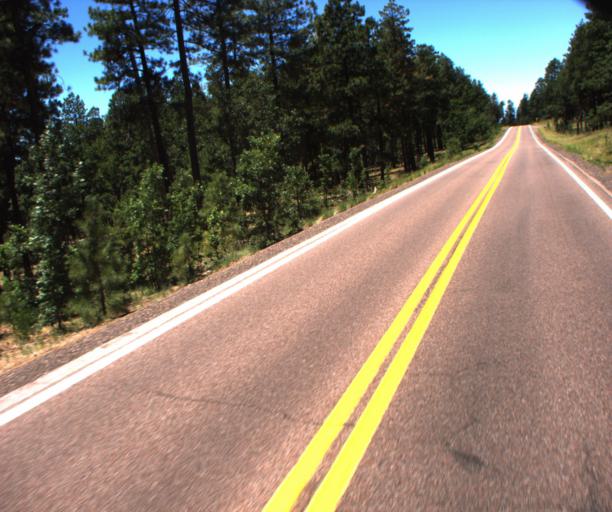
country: US
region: Arizona
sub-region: Gila County
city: Pine
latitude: 34.4418
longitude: -111.4580
